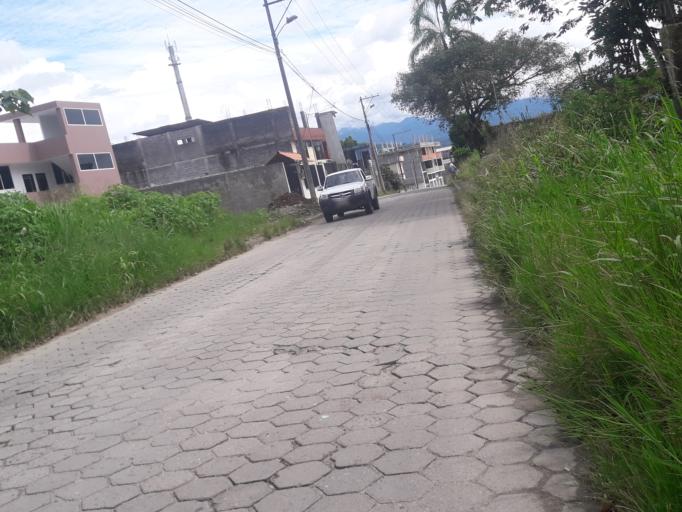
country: EC
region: Napo
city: Tena
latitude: -1.0034
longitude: -77.8102
